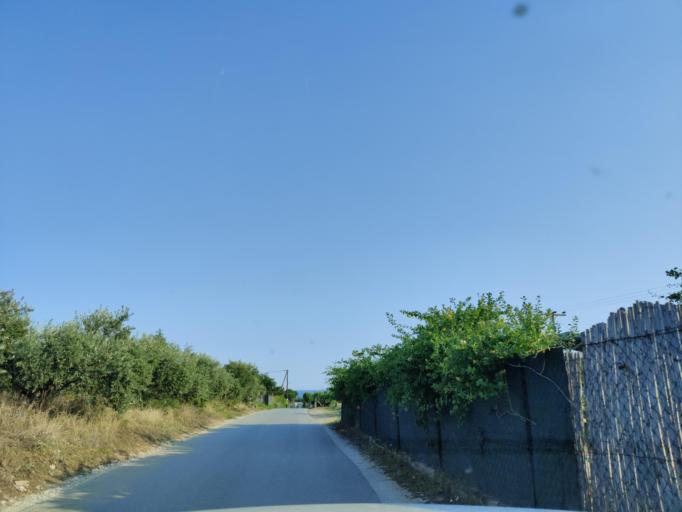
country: GR
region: East Macedonia and Thrace
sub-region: Nomos Kavalas
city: Nea Peramos
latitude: 40.8175
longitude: 24.2865
